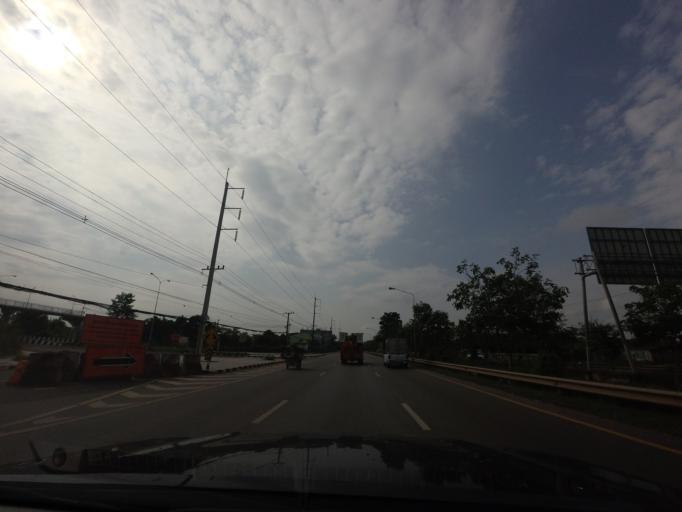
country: TH
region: Nong Khai
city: Nong Khai
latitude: 17.8571
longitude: 102.7502
